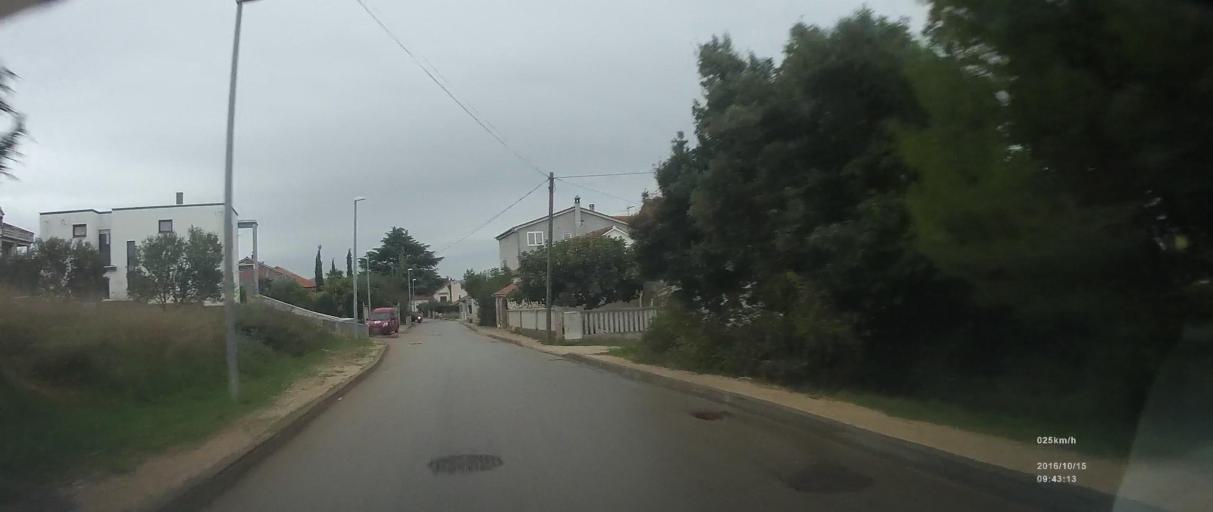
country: HR
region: Zadarska
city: Pakostane
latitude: 43.9117
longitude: 15.5035
